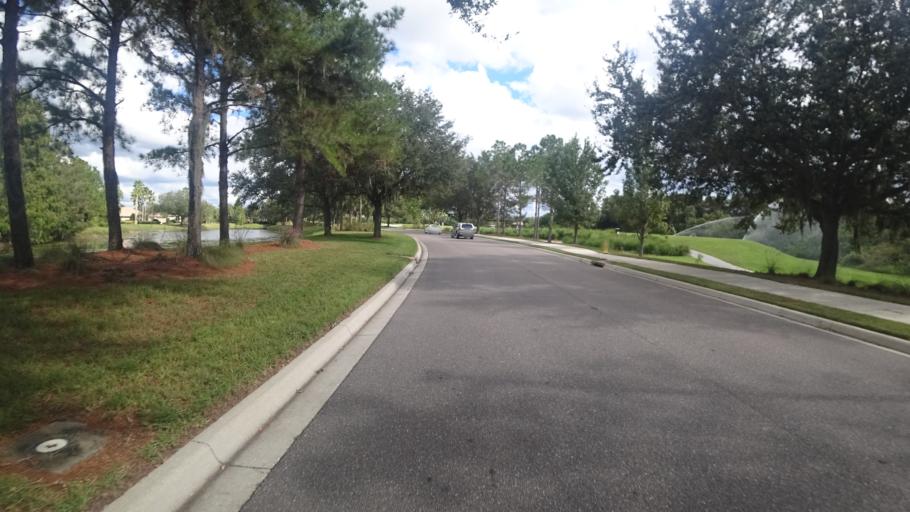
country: US
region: Florida
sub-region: Sarasota County
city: The Meadows
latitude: 27.3942
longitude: -82.4090
